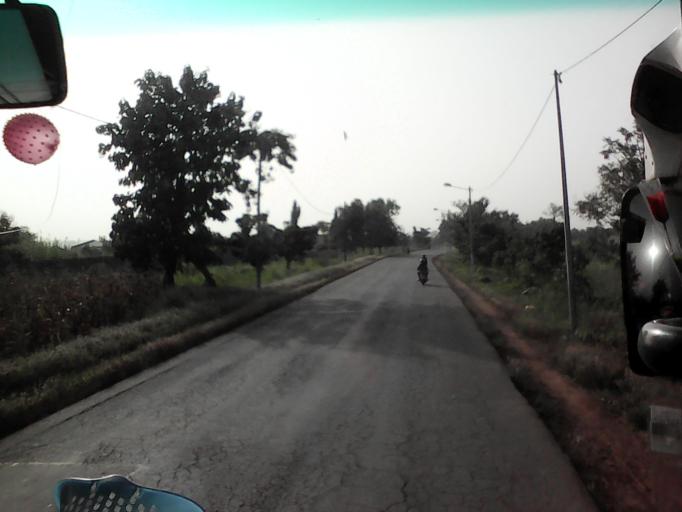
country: TG
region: Kara
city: Kara
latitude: 9.5256
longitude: 1.2062
